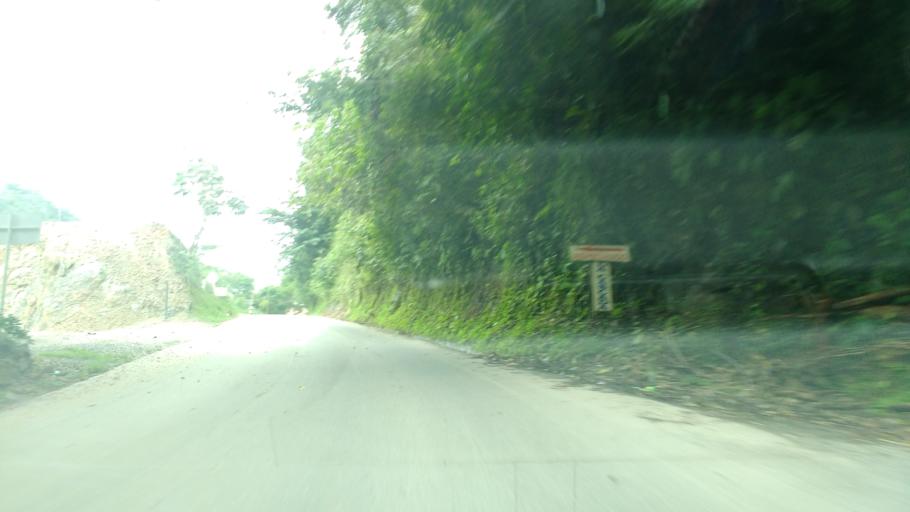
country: CO
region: Antioquia
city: Amaga
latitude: 6.0496
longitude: -75.7211
